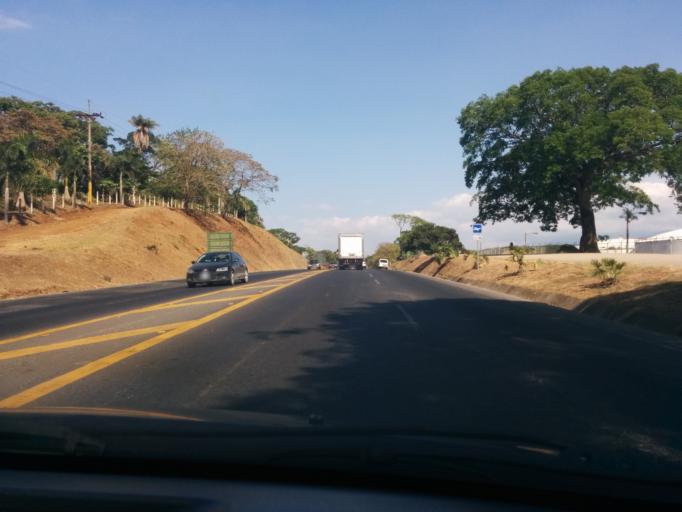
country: CR
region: Alajuela
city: Carrillos
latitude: 10.0052
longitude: -84.2933
